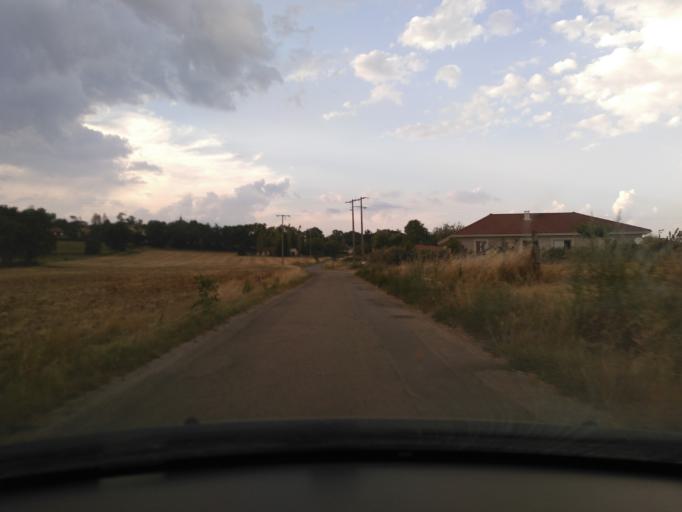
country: FR
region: Rhone-Alpes
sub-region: Departement de l'Isere
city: Beaurepaire
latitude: 45.3814
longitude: 4.9937
